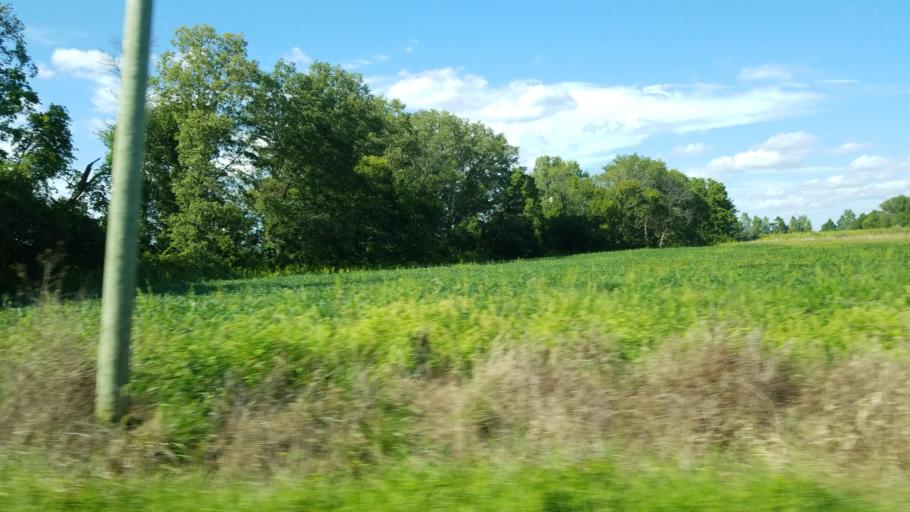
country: US
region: Illinois
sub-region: Saline County
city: Harrisburg
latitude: 37.8127
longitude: -88.5628
